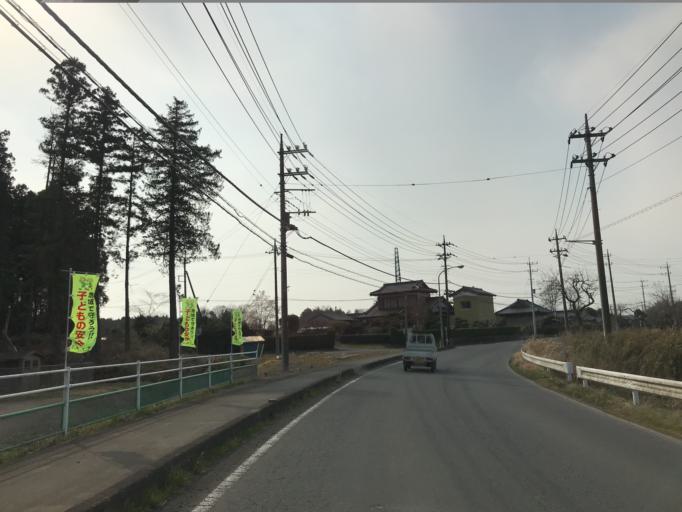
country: JP
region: Ibaraki
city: Okunoya
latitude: 36.2350
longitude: 140.3693
